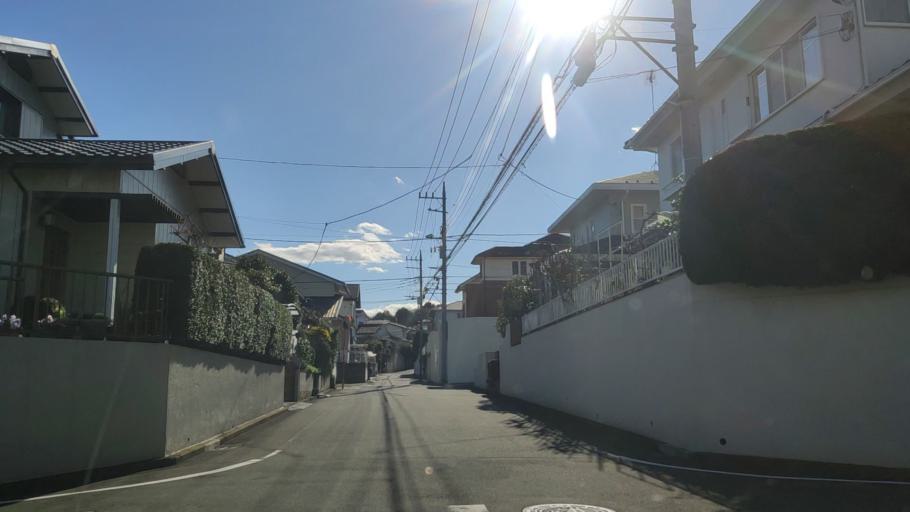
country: JP
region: Kanagawa
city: Minami-rinkan
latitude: 35.5078
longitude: 139.5254
